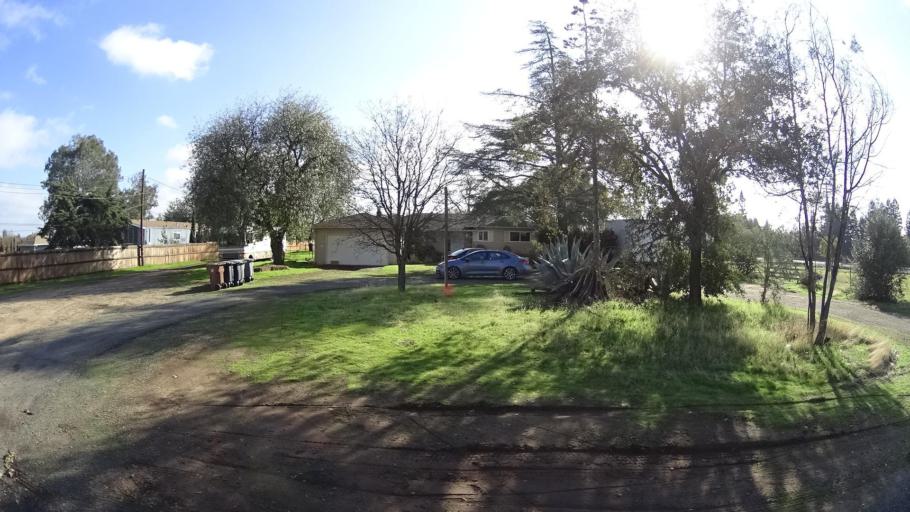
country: US
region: California
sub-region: Sacramento County
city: Elk Grove
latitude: 38.4290
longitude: -121.3708
